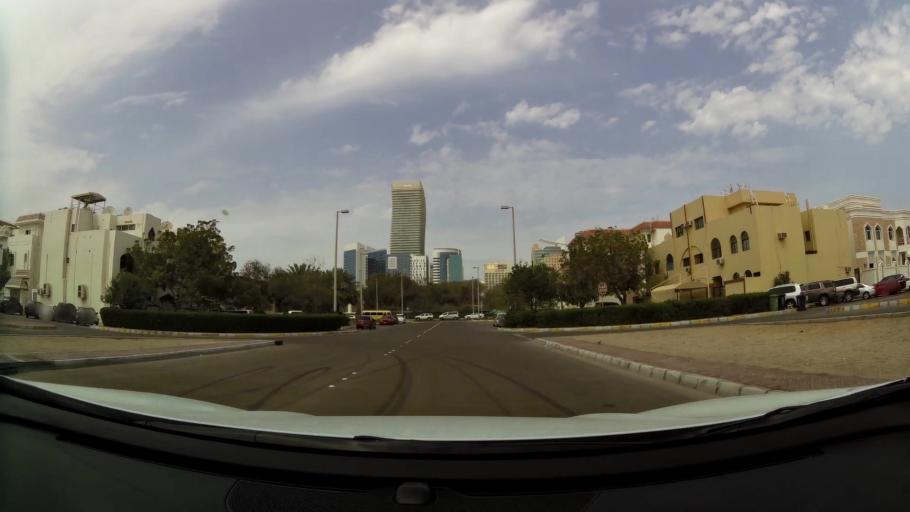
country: AE
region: Abu Dhabi
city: Abu Dhabi
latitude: 24.4647
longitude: 54.3444
